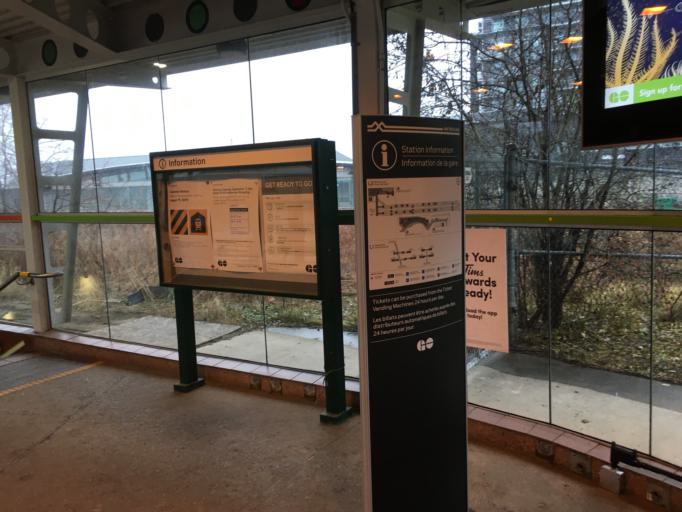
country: CA
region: Ontario
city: Burlington
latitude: 43.3404
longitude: -79.8112
